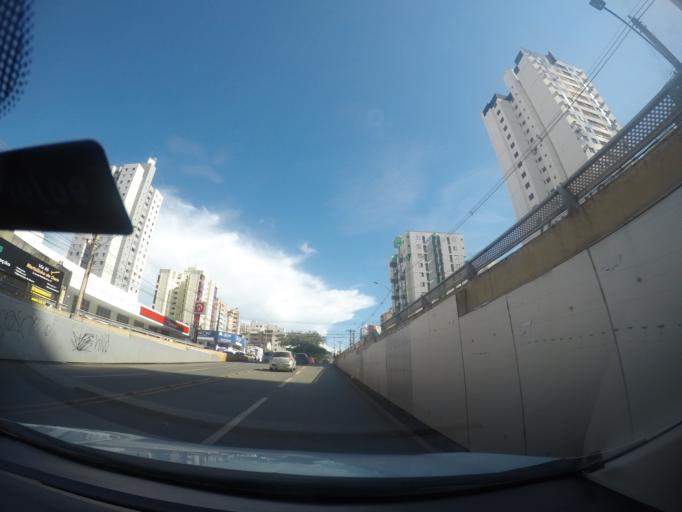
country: BR
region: Goias
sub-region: Goiania
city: Goiania
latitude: -16.7152
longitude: -49.2636
